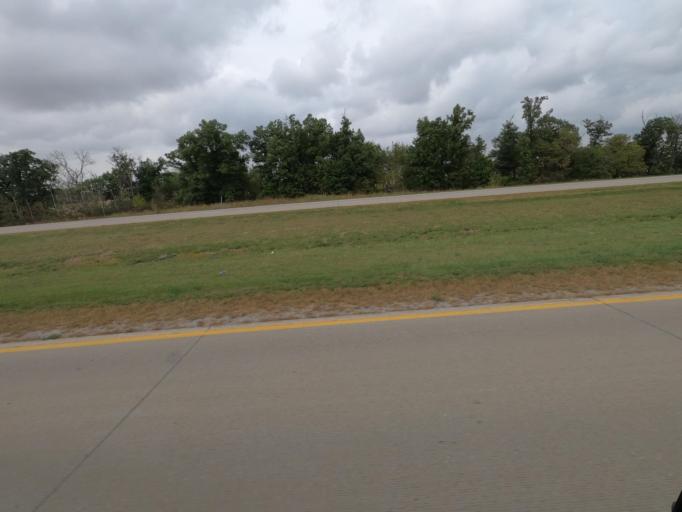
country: US
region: Iowa
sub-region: Wapello County
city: Ottumwa
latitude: 41.0018
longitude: -92.2678
